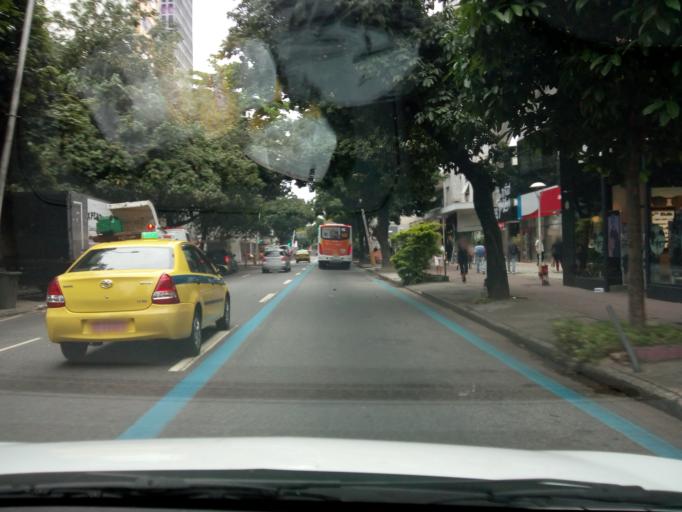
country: BR
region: Rio de Janeiro
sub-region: Rio De Janeiro
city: Rio de Janeiro
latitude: -22.9838
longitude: -43.2106
